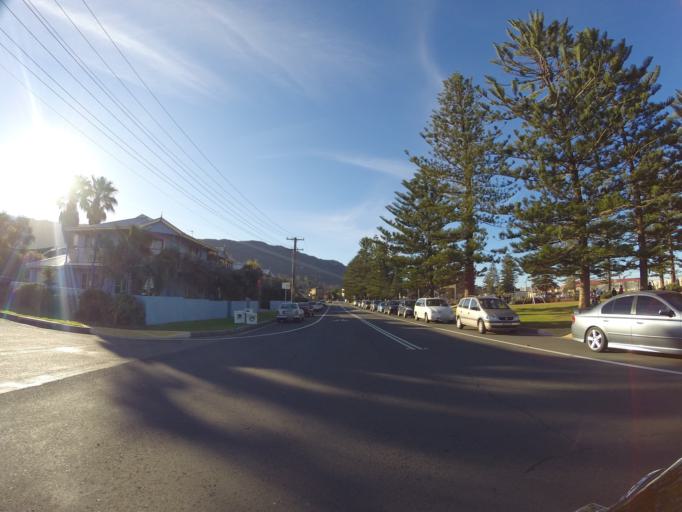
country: AU
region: New South Wales
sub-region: Wollongong
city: Bulli
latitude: -34.3173
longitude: 150.9261
